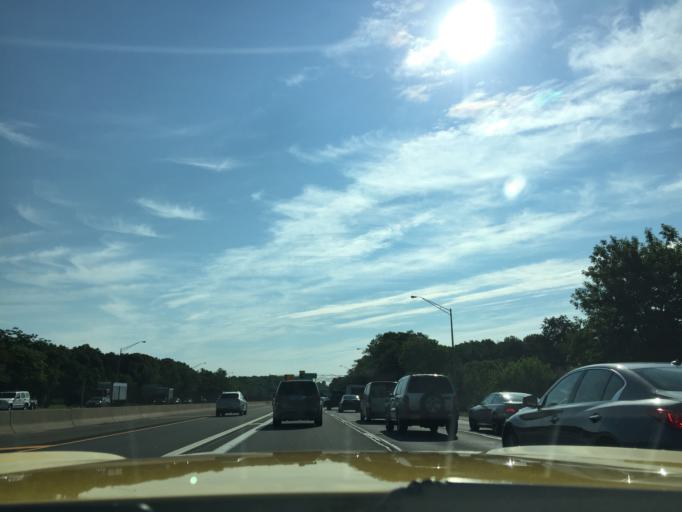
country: US
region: New York
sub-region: Suffolk County
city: Melville
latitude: 40.7853
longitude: -73.3935
